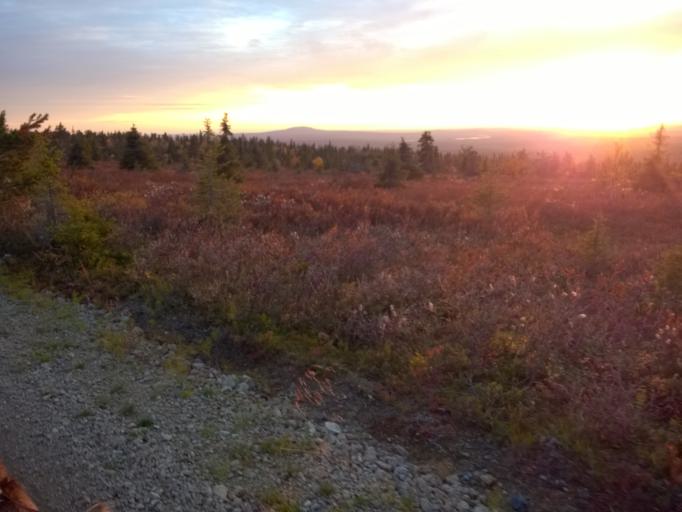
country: FI
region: Lapland
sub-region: Tunturi-Lappi
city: Muonio
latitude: 67.9745
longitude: 24.1007
